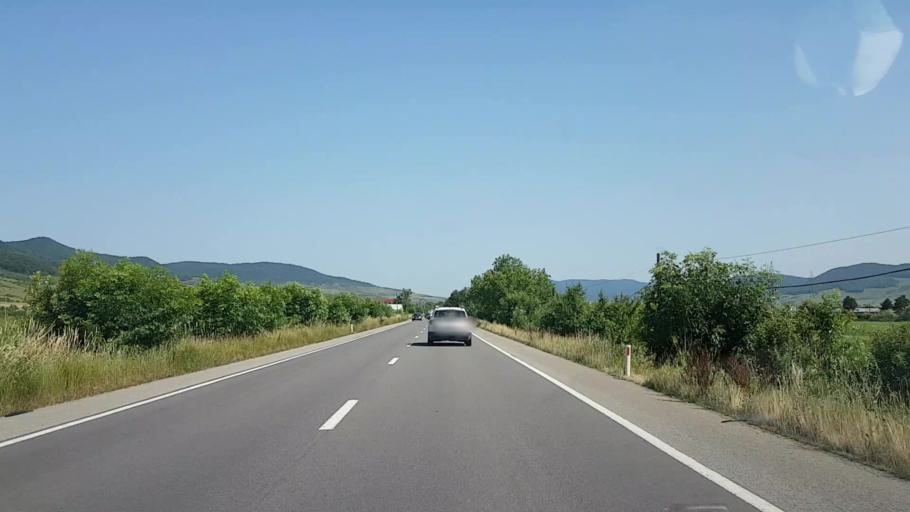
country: RO
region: Bistrita-Nasaud
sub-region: Comuna Sieu-Magherus
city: Sieu-Magherus
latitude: 47.1031
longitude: 24.3566
